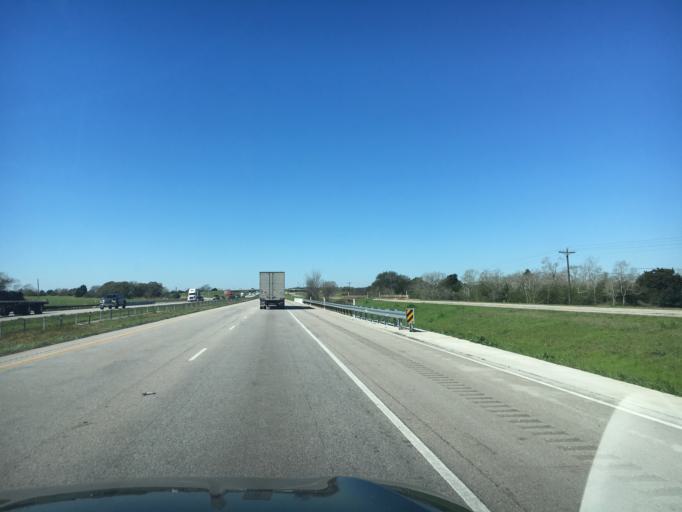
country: US
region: Texas
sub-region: Colorado County
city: Eagle Lake
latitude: 29.7308
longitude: -96.3840
